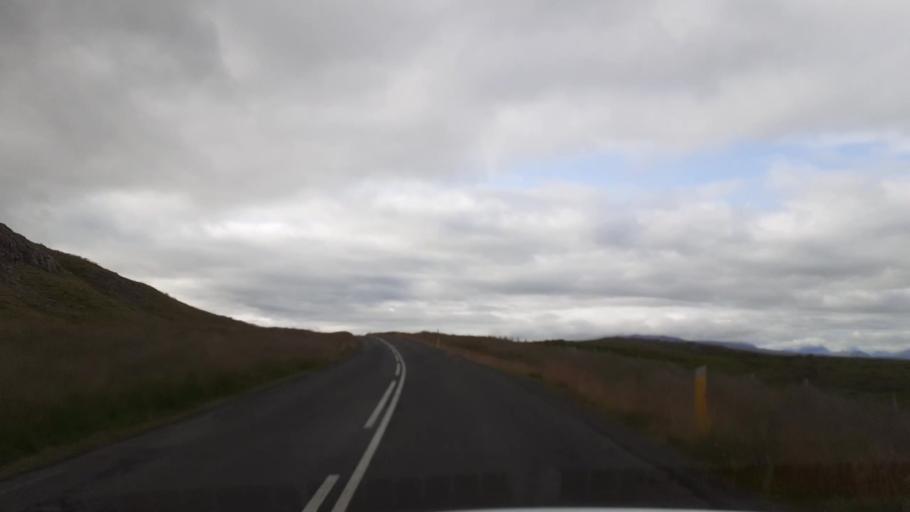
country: IS
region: Northeast
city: Akureyri
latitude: 65.8087
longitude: -18.0557
